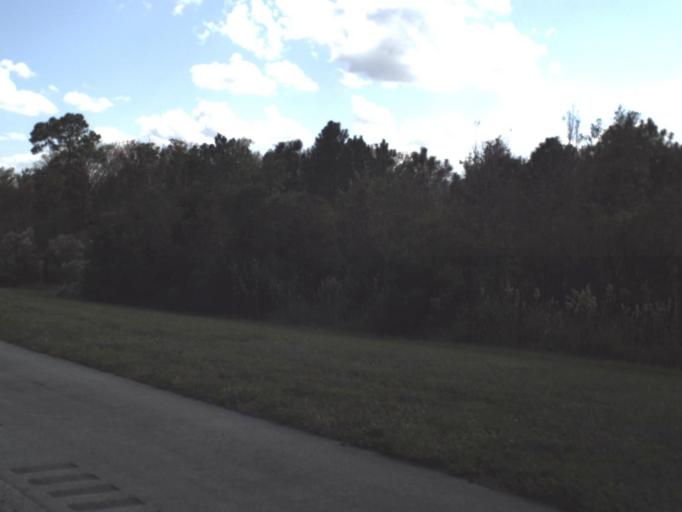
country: US
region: Florida
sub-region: Indian River County
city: Fellsmere
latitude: 27.7304
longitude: -80.9161
